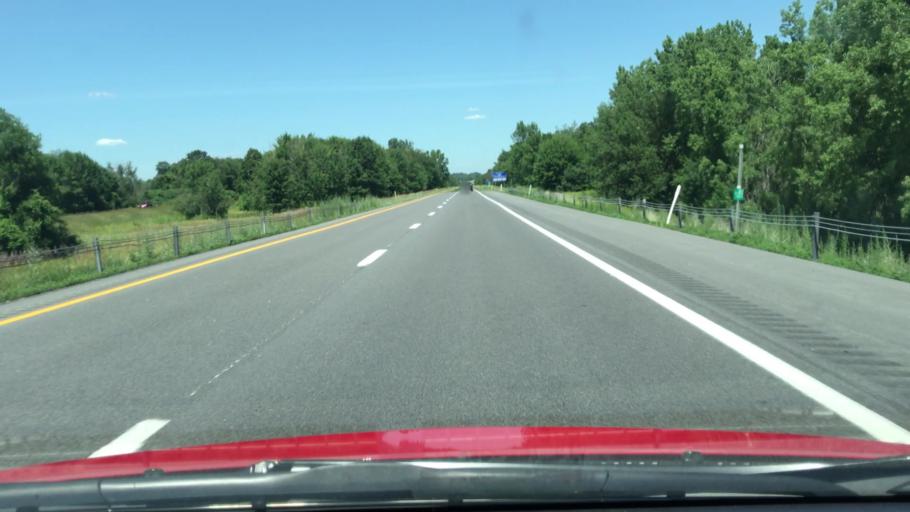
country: US
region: New York
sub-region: Clinton County
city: Cumberland Head
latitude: 44.7645
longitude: -73.4316
